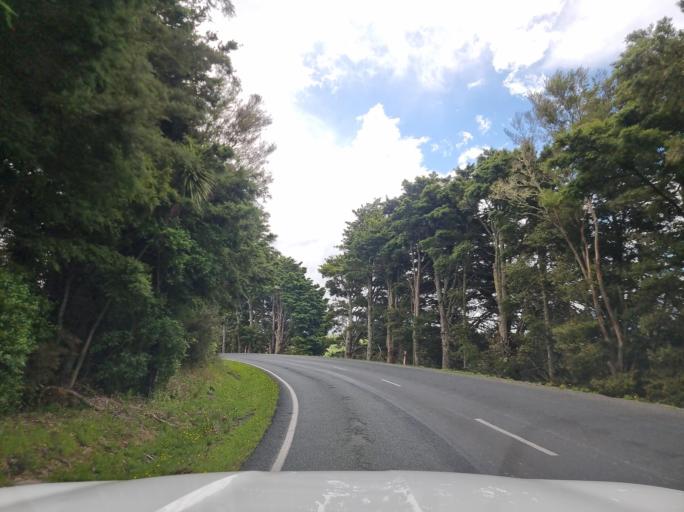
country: NZ
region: Northland
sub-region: Whangarei
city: Ruakaka
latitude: -35.9243
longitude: 174.2803
